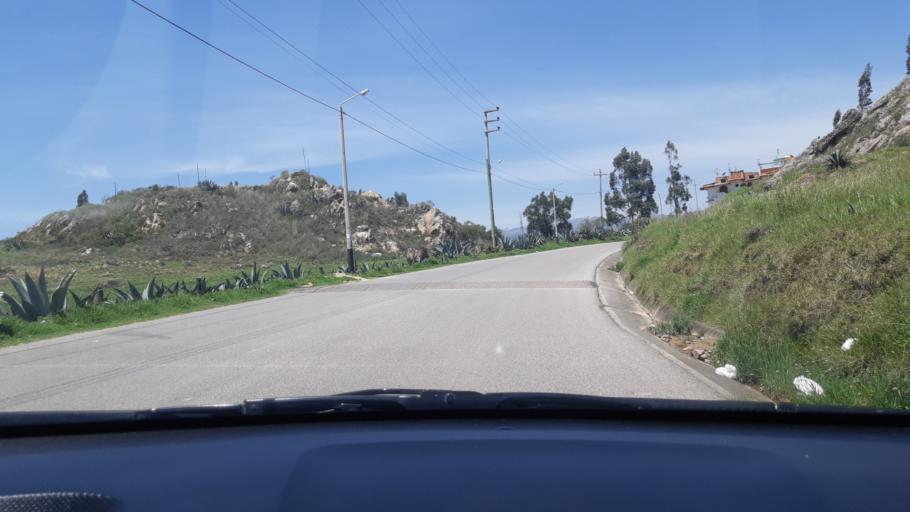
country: PE
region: Cajamarca
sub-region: Provincia de Cajamarca
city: Llacanora
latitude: -7.1752
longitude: -78.4581
